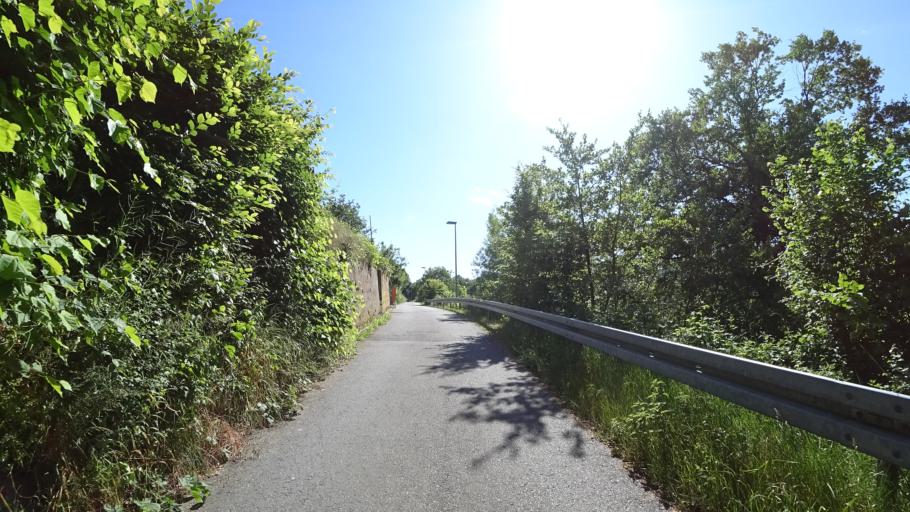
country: DE
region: Bavaria
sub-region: Regierungsbezirk Unterfranken
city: Kleinheubach
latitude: 49.7021
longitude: 9.2332
